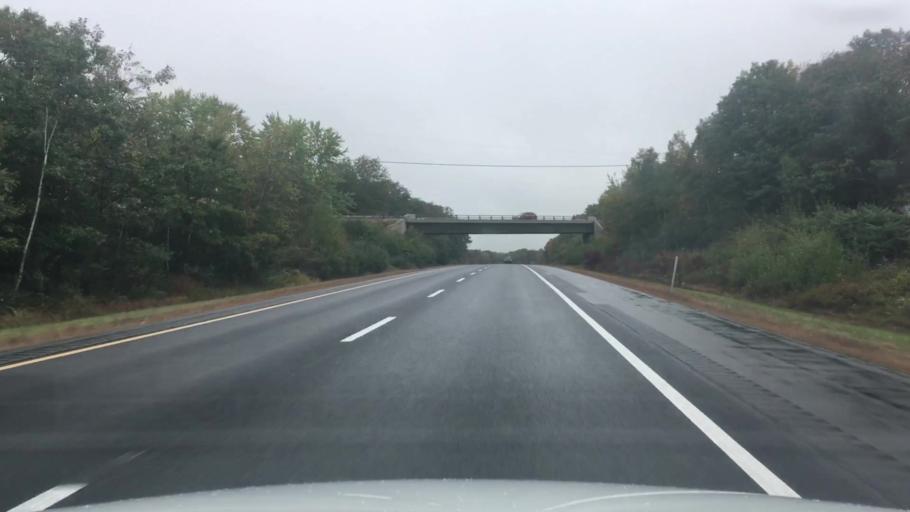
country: US
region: Maine
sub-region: Kennebec County
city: Gardiner
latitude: 44.1774
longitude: -69.8332
